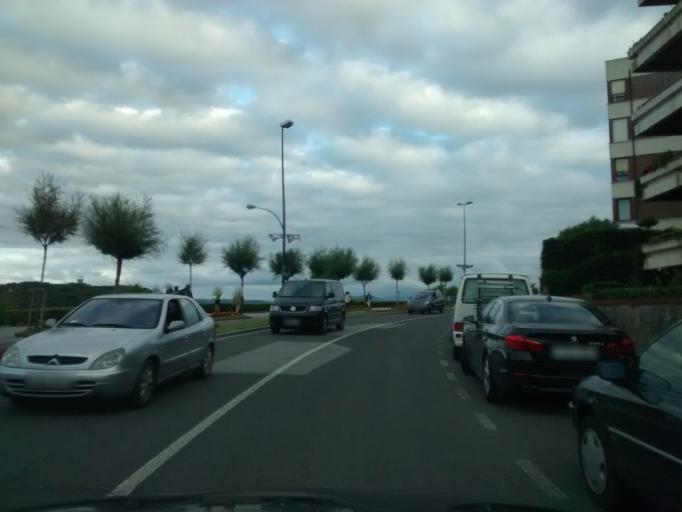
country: ES
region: Cantabria
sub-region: Provincia de Cantabria
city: Santander
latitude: 43.4709
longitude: -3.7781
